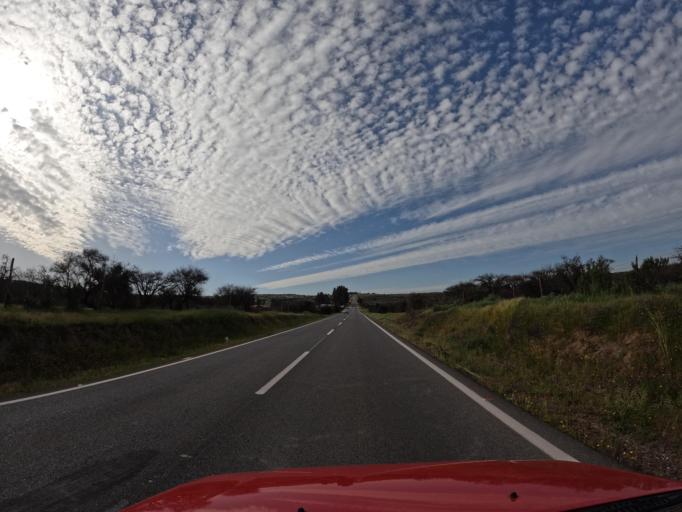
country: CL
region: O'Higgins
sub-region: Provincia de Colchagua
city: Santa Cruz
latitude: -34.2821
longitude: -71.7296
